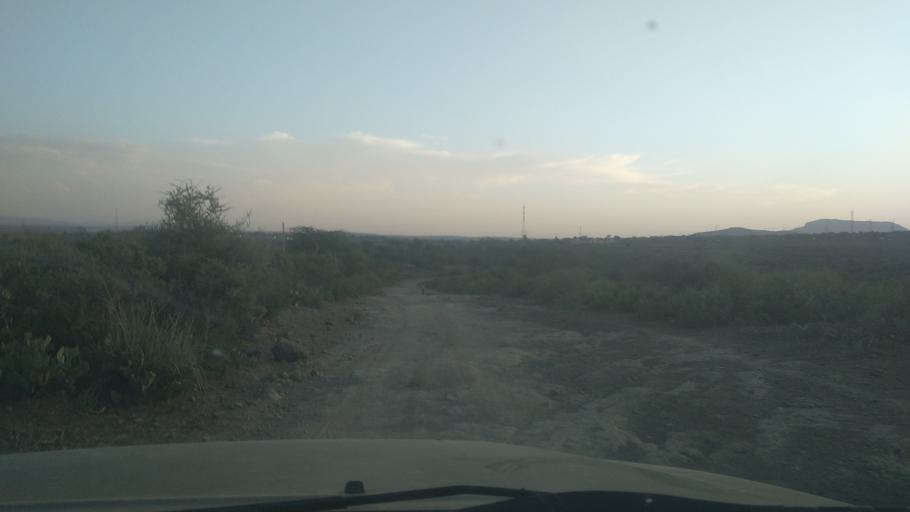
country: ET
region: Oromiya
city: Asbe Teferi
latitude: 9.2432
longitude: 40.7703
